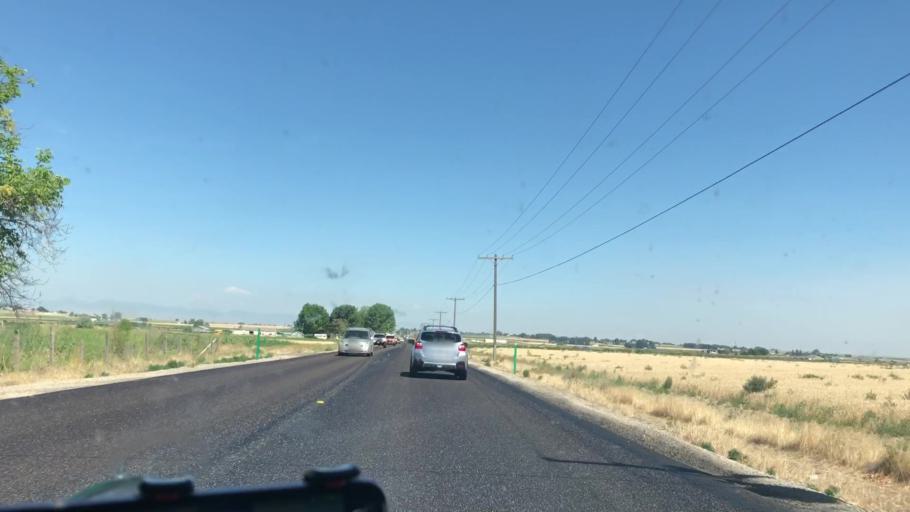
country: US
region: Idaho
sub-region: Owyhee County
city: Marsing
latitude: 43.6031
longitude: -116.7700
